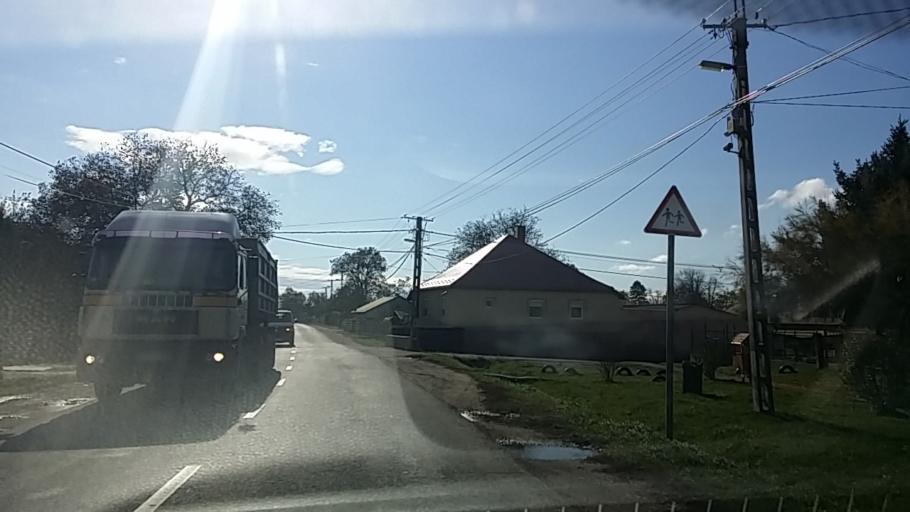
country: HU
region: Borsod-Abauj-Zemplen
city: Gonc
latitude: 48.4152
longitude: 21.2308
